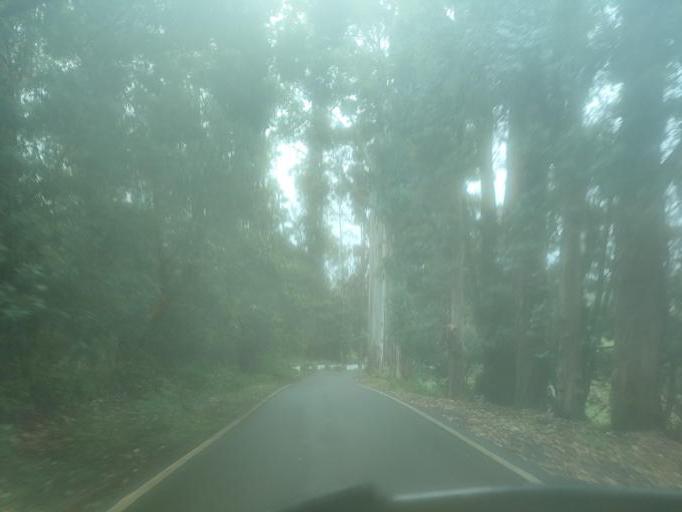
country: IN
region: Tamil Nadu
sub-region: Dindigul
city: Kodaikanal
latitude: 10.2078
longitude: 77.3493
